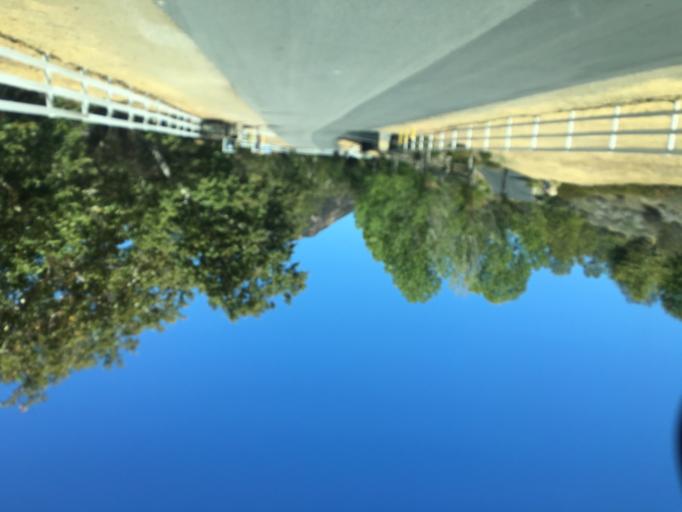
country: US
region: California
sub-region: Los Angeles County
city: Westlake Village
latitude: 34.1189
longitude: -118.8083
